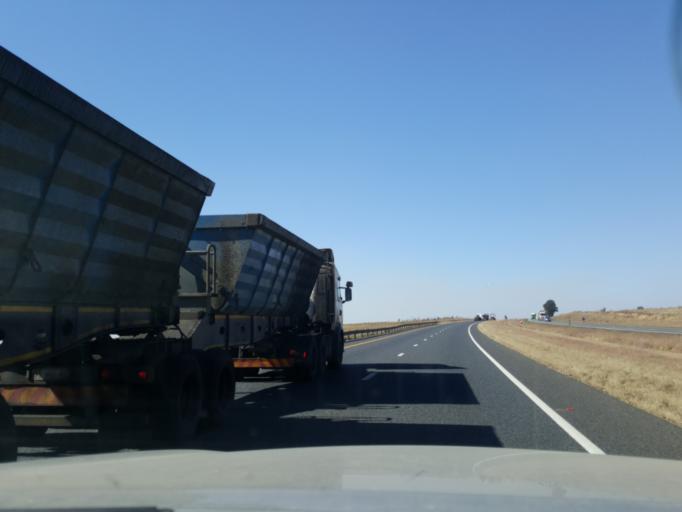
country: ZA
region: Mpumalanga
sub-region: Nkangala District Municipality
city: Delmas
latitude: -26.0185
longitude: 28.9023
